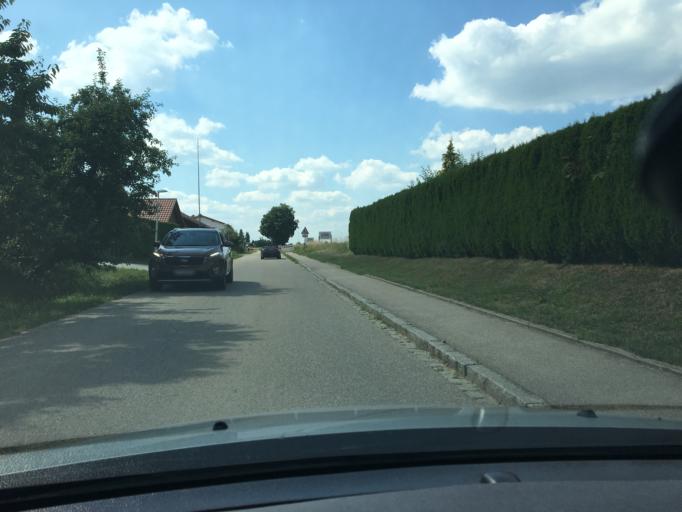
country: DE
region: Bavaria
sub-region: Lower Bavaria
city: Vilsheim
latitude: 48.4482
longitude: 12.1009
